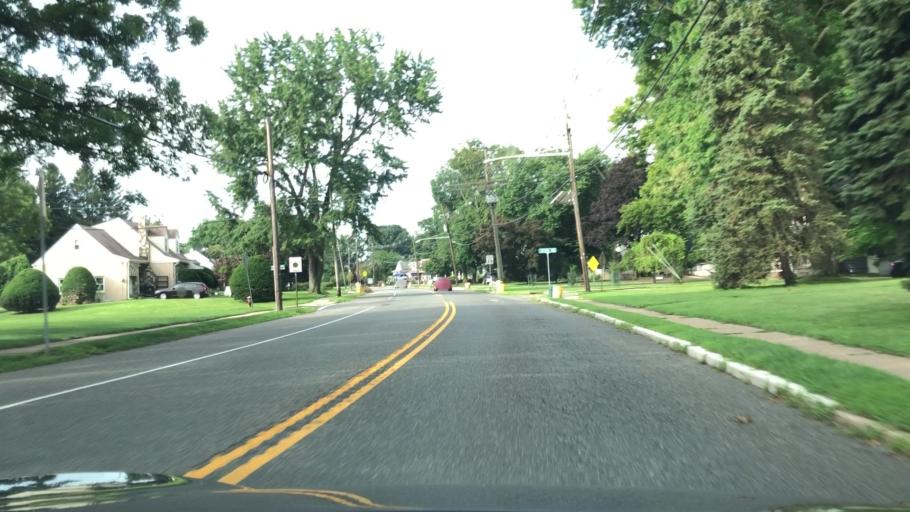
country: US
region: New Jersey
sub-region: Mercer County
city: Lawrenceville
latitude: 40.2695
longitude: -74.7396
